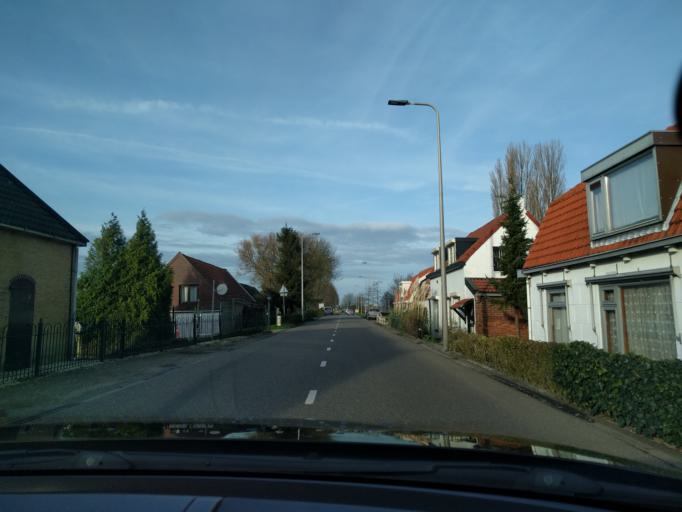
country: NL
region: South Holland
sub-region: Gemeente Spijkenisse
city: Spijkenisse
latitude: 51.8261
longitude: 4.2585
